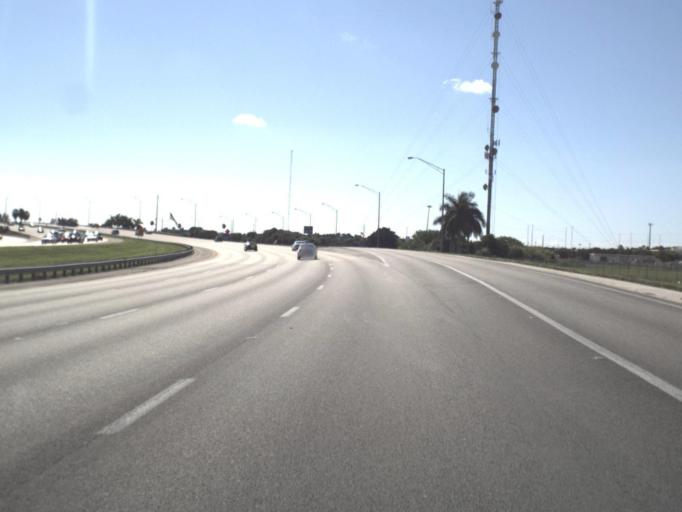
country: US
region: Florida
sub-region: Miami-Dade County
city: Three Lakes
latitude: 25.6347
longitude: -80.3854
